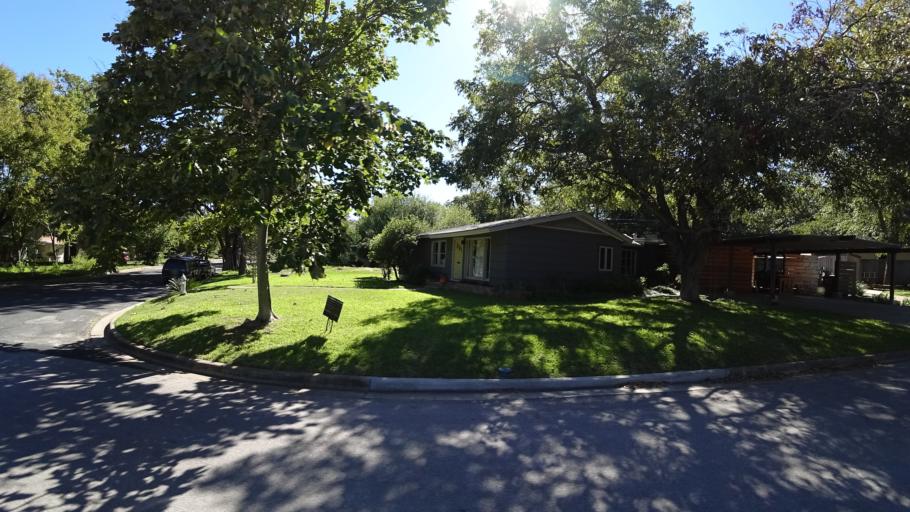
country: US
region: Texas
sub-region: Travis County
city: West Lake Hills
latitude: 30.3274
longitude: -97.7532
